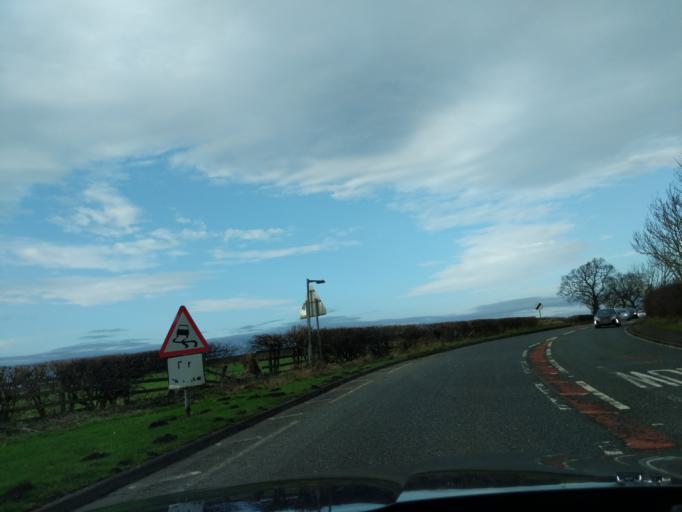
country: GB
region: England
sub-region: Northumberland
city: Ponteland
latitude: 55.0502
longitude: -1.7563
